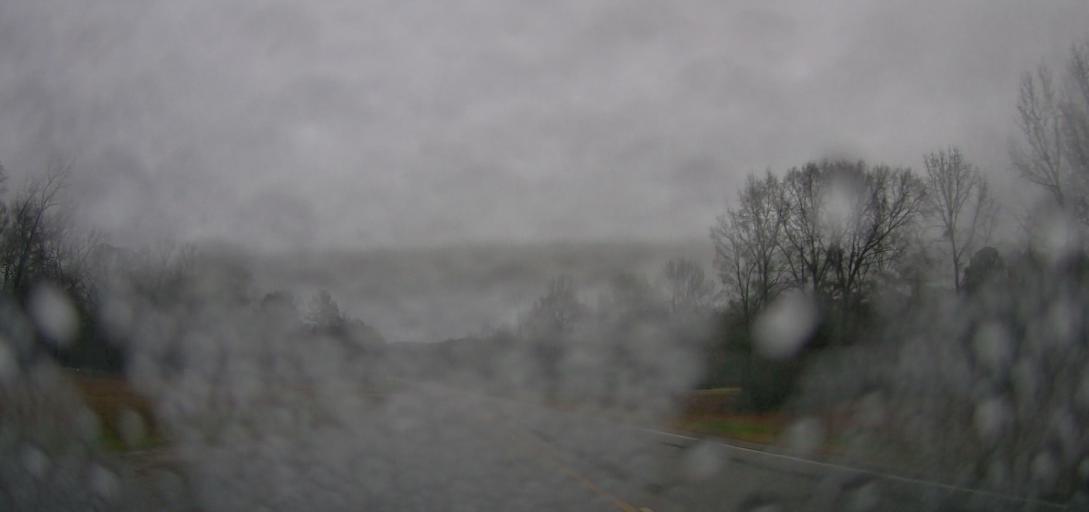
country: US
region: Alabama
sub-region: Autauga County
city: Prattville
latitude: 32.4981
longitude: -86.5823
